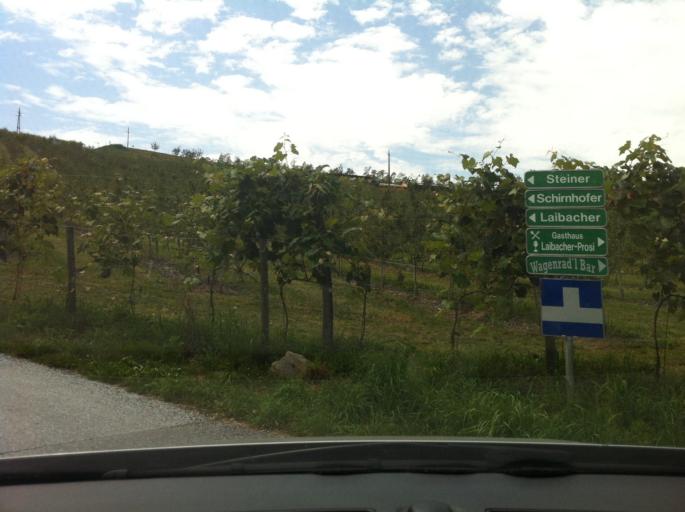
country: AT
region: Styria
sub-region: Politischer Bezirk Hartberg-Fuerstenfeld
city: Stubenberg
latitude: 47.2490
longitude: 15.7886
